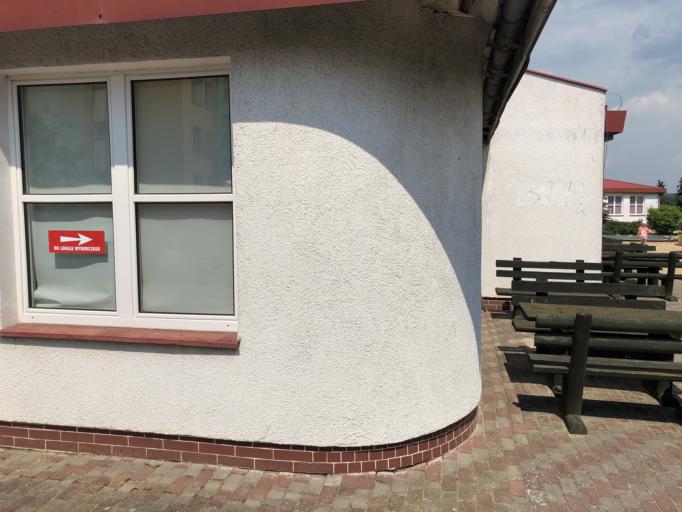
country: PL
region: Pomeranian Voivodeship
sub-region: Powiat kwidzynski
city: Kwidzyn
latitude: 53.7382
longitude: 18.9486
